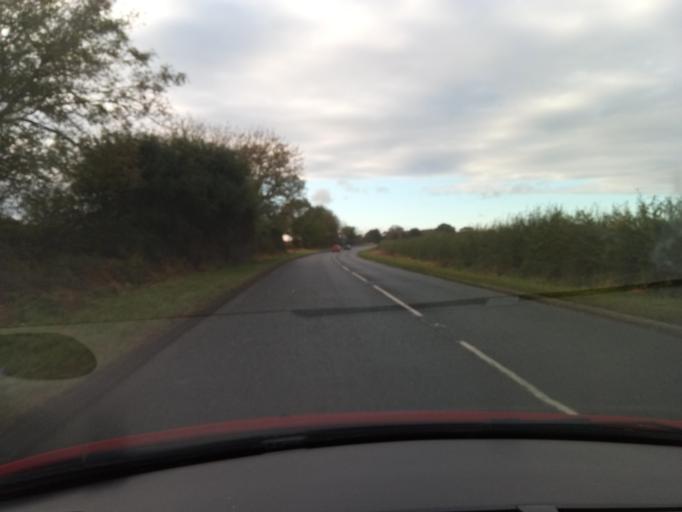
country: GB
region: England
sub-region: Darlington
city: Heighington
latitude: 54.5812
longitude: -1.6223
